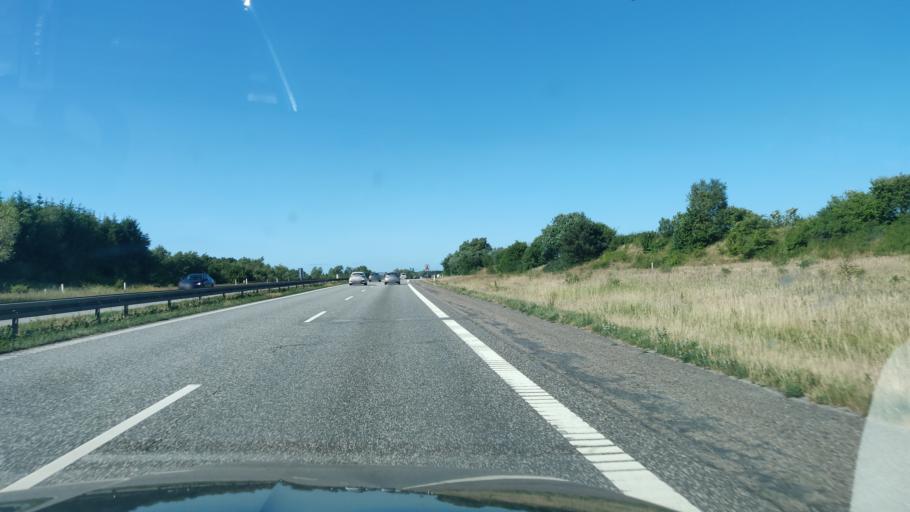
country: DK
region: North Denmark
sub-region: Mariagerfjord Kommune
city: Hobro
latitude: 56.6254
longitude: 9.7332
